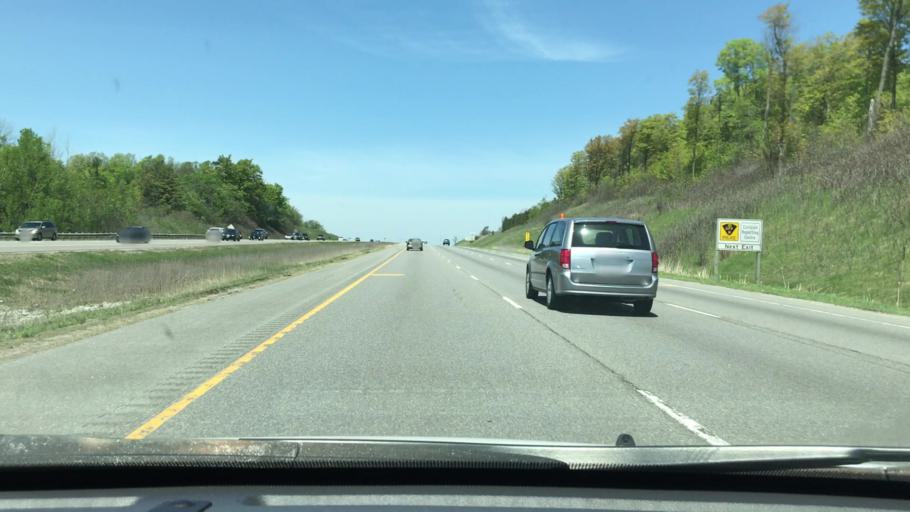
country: CA
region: Ontario
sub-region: York
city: Richmond Hill
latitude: 43.9668
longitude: -79.3926
